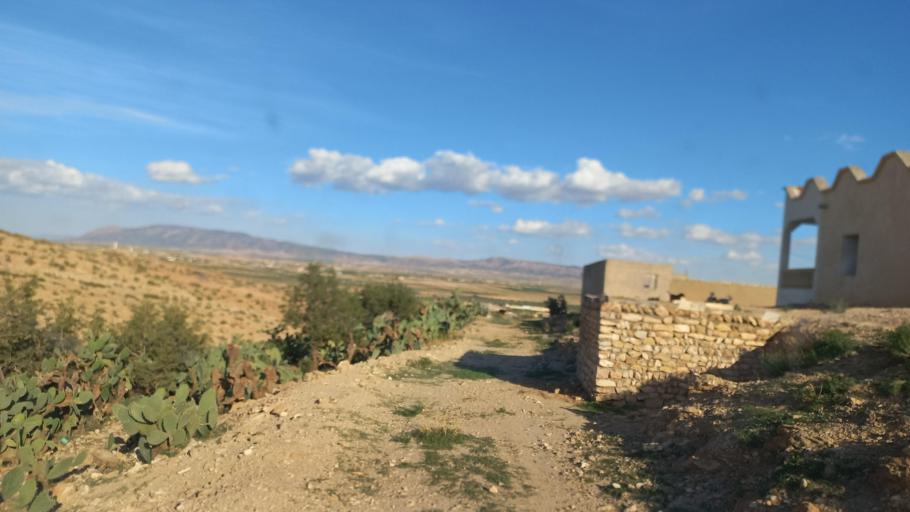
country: TN
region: Al Qasrayn
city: Sbiba
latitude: 35.3831
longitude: 9.0180
